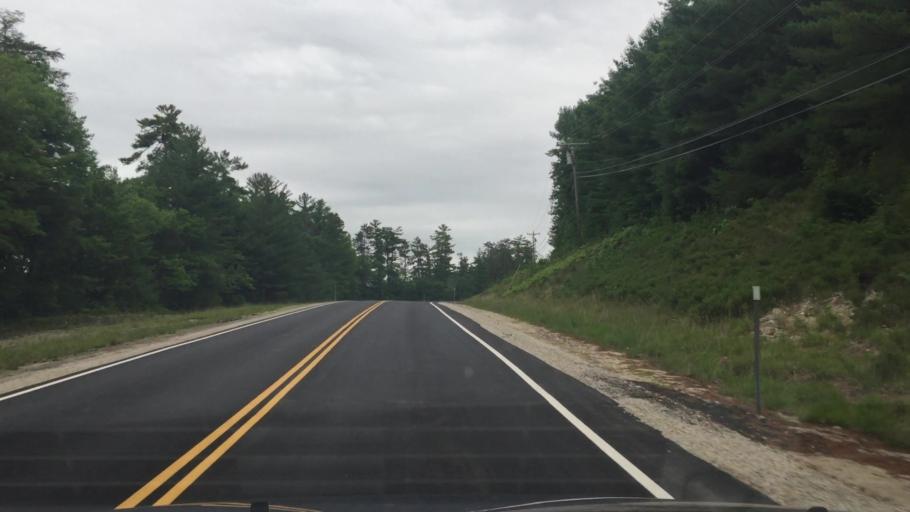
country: US
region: New Hampshire
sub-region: Carroll County
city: Madison
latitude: 43.8723
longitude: -71.0867
